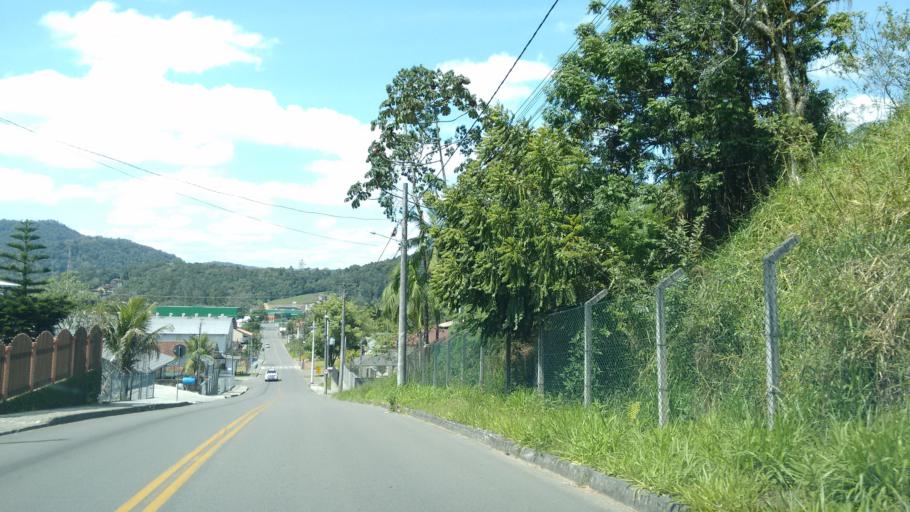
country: BR
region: Santa Catarina
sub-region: Pomerode
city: Pomerode
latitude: -26.7178
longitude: -49.1756
